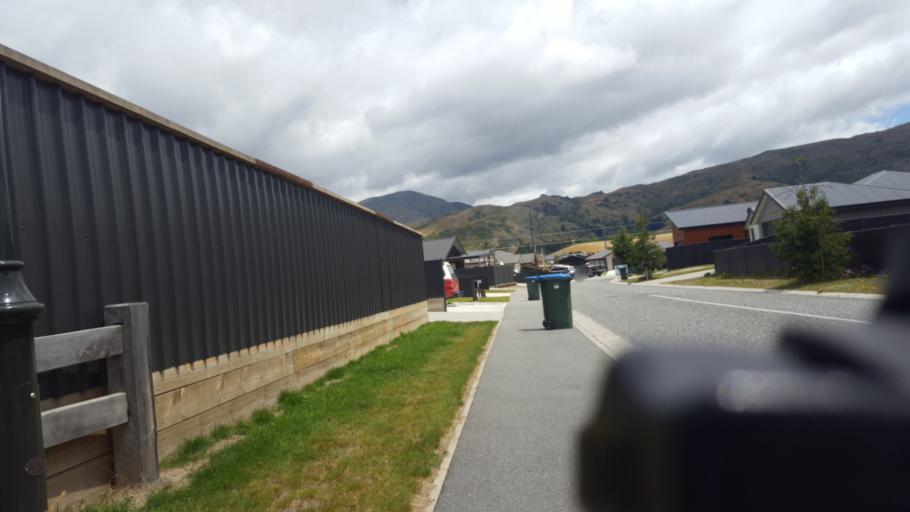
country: NZ
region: Otago
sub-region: Queenstown-Lakes District
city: Wanaka
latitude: -45.0472
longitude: 169.1795
